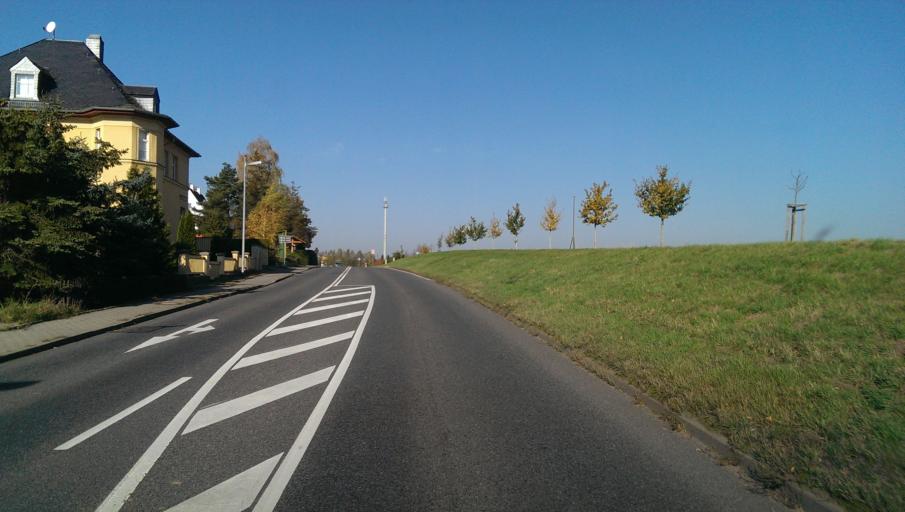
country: DE
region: Saxony
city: Mittweida
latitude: 50.9988
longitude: 12.9585
